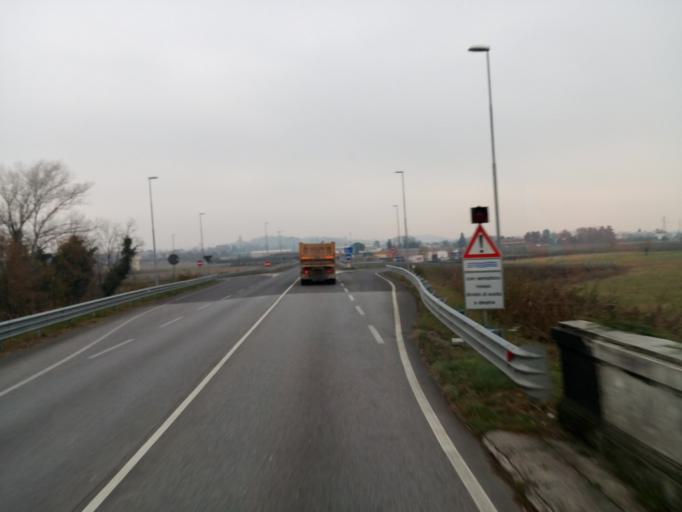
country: IT
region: Friuli Venezia Giulia
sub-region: Provincia di Udine
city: Pradamano
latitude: 46.0163
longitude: 13.3131
